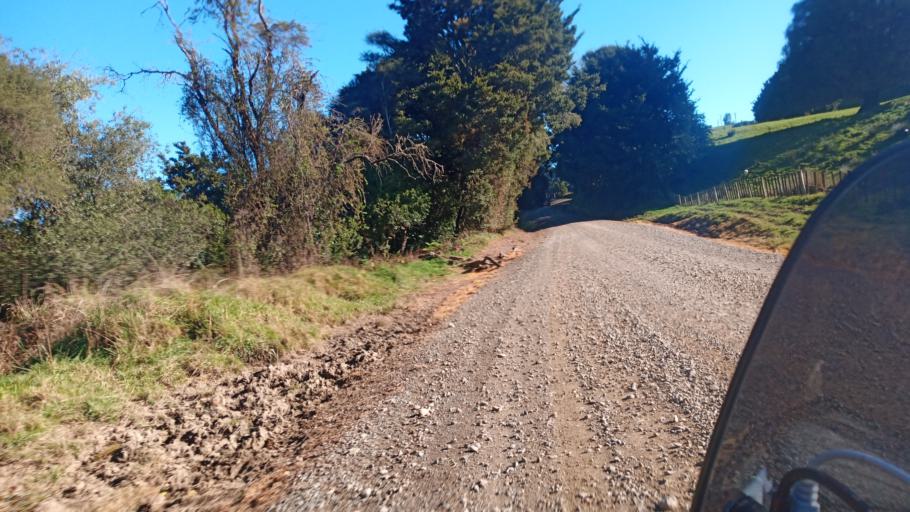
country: NZ
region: Hawke's Bay
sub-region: Wairoa District
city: Wairoa
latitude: -38.8164
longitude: 177.2919
